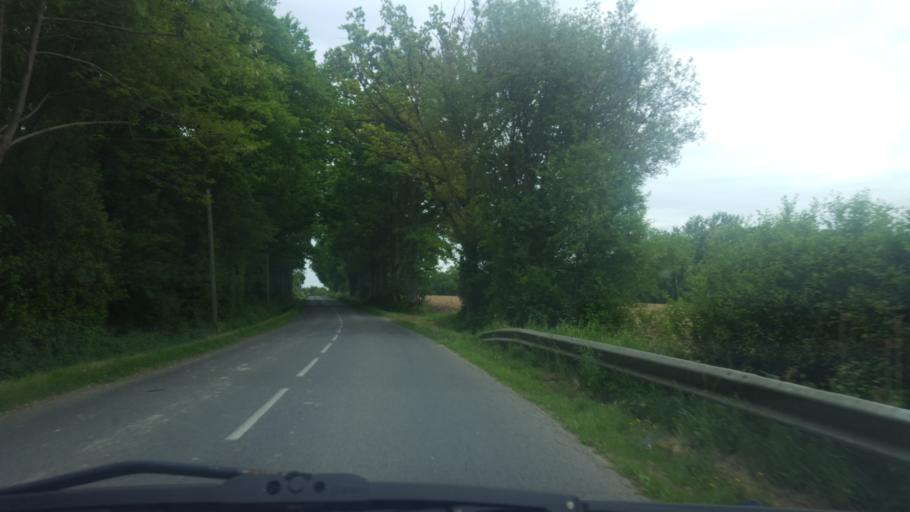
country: FR
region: Pays de la Loire
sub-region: Departement de la Loire-Atlantique
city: Geneston
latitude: 47.0287
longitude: -1.5523
